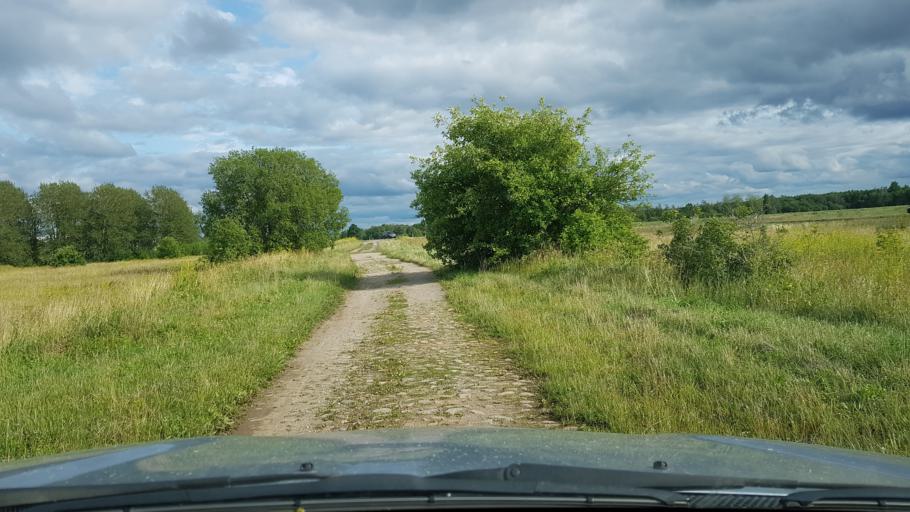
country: EE
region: Ida-Virumaa
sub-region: Narva-Joesuu linn
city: Narva-Joesuu
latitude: 59.4012
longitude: 28.0684
